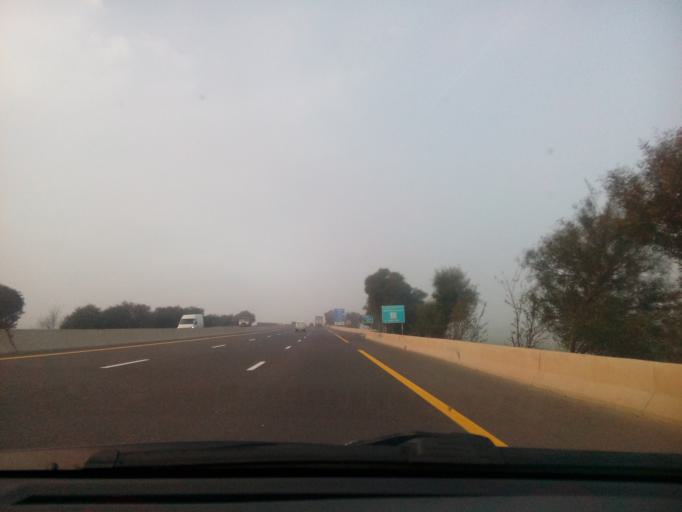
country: DZ
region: Relizane
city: Relizane
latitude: 35.7968
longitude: 0.5006
